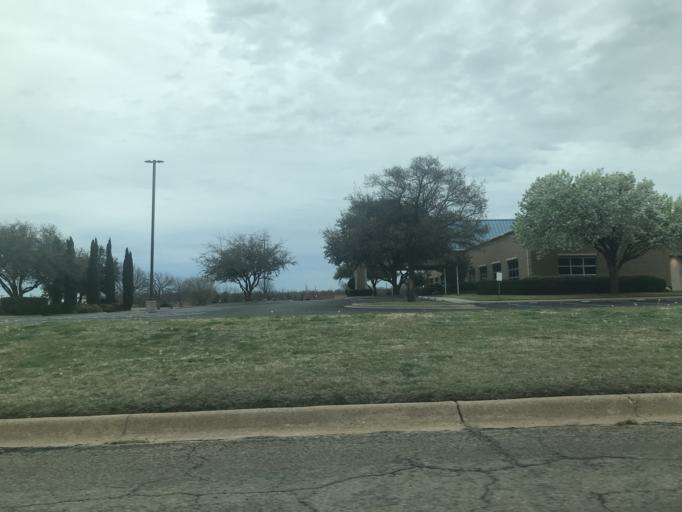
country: US
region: Texas
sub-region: Taylor County
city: Abilene
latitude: 32.4696
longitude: -99.7287
